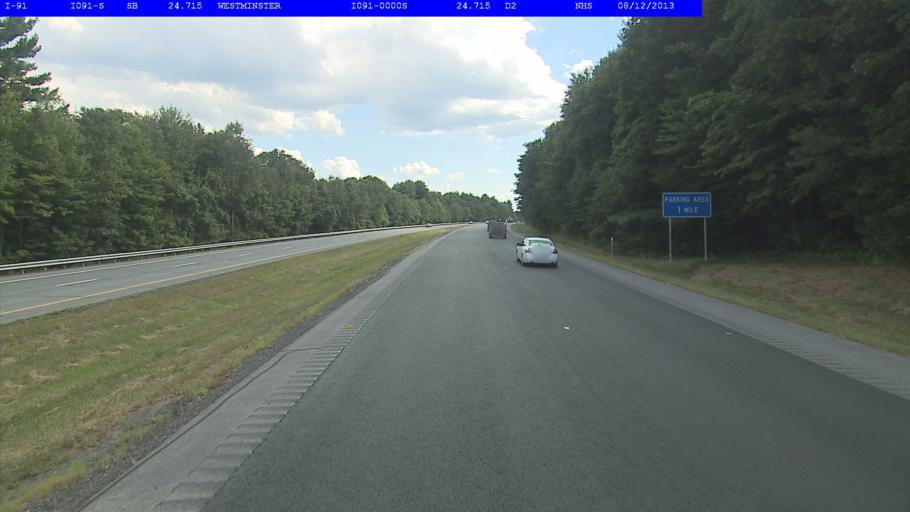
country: US
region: New Hampshire
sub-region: Cheshire County
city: Westmoreland
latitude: 43.0370
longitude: -72.4689
